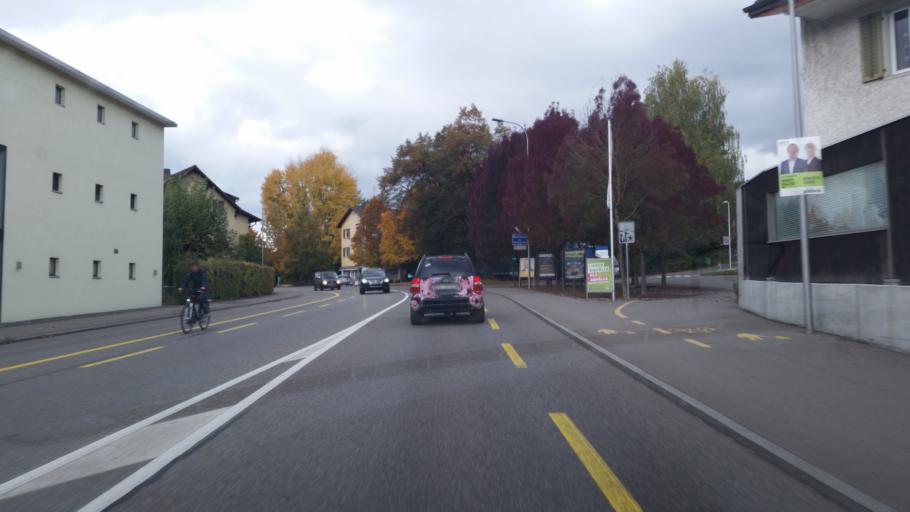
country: CH
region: Aargau
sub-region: Bezirk Baden
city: Obersiggenthal
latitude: 47.4857
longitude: 8.2986
